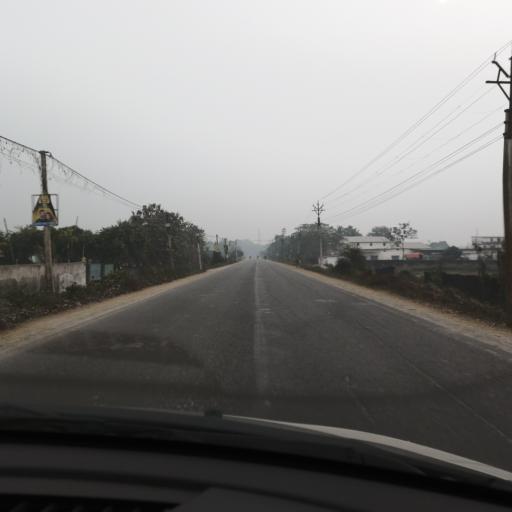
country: IN
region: West Bengal
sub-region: Darjiling
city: Shiliguri
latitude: 26.6758
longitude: 88.4658
